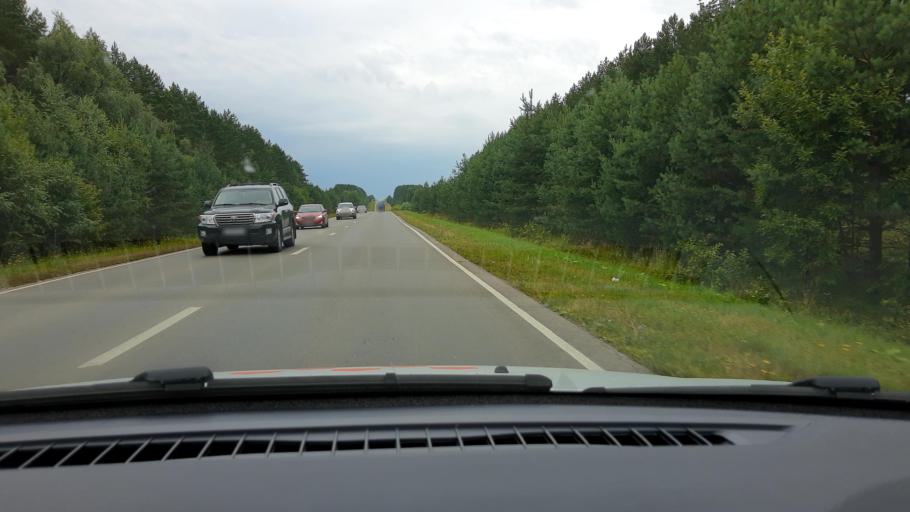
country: RU
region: Nizjnij Novgorod
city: Vyyezdnoye
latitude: 55.1642
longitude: 43.5868
